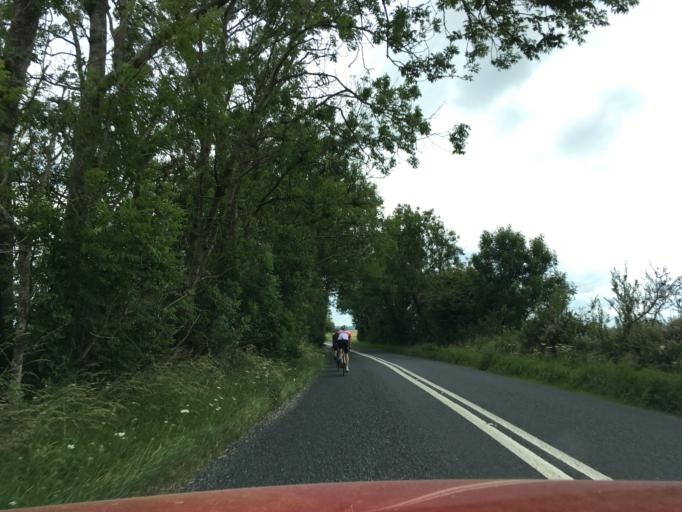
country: GB
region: England
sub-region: Gloucestershire
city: Westfield
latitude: 51.8875
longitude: -1.8435
